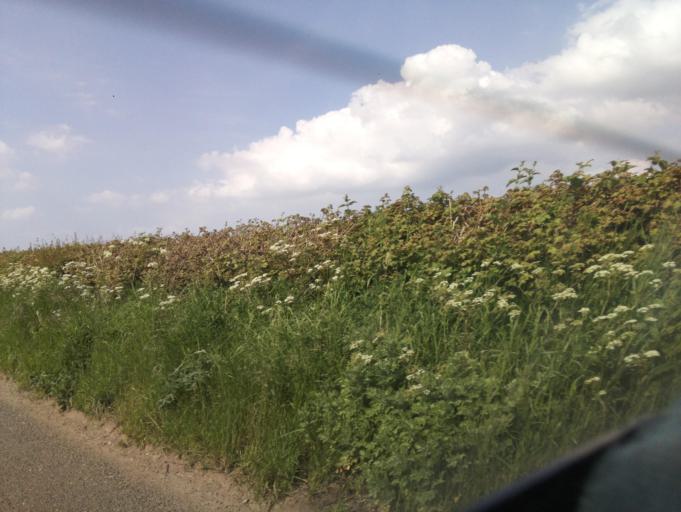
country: GB
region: England
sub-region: Wiltshire
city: Norton
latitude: 51.5497
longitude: -2.1527
